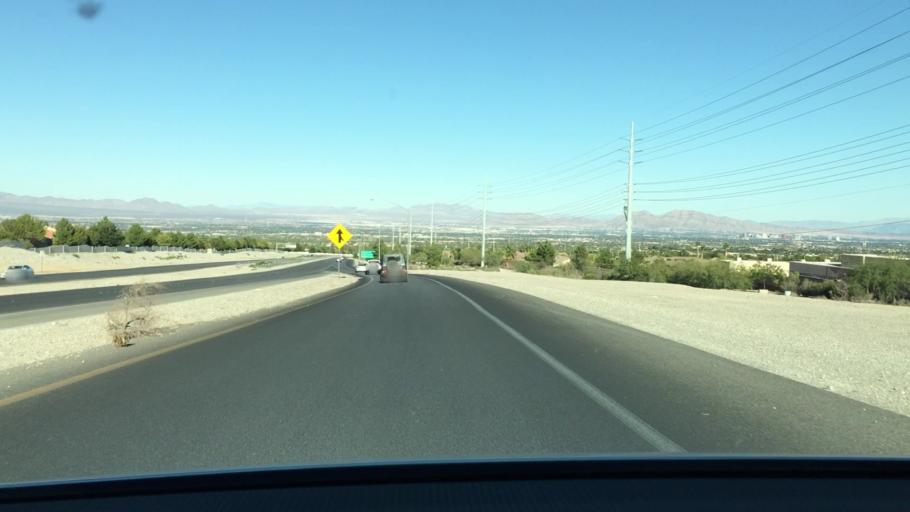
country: US
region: Nevada
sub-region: Clark County
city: Summerlin South
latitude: 36.1913
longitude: -115.3378
